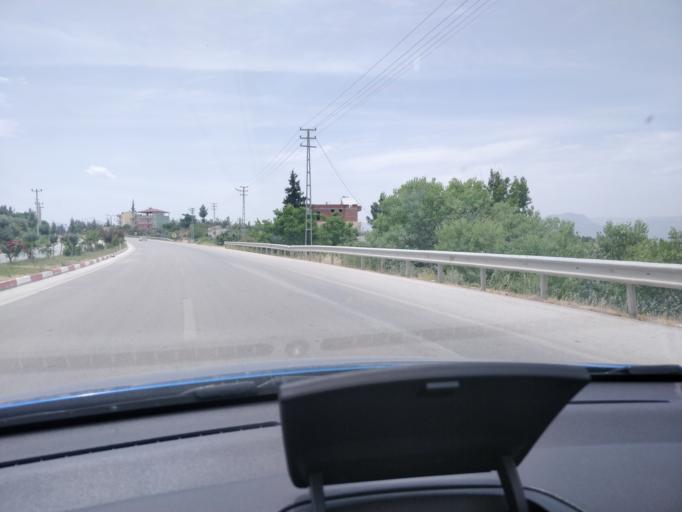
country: TR
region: Mersin
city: Mut
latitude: 36.6202
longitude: 33.4423
